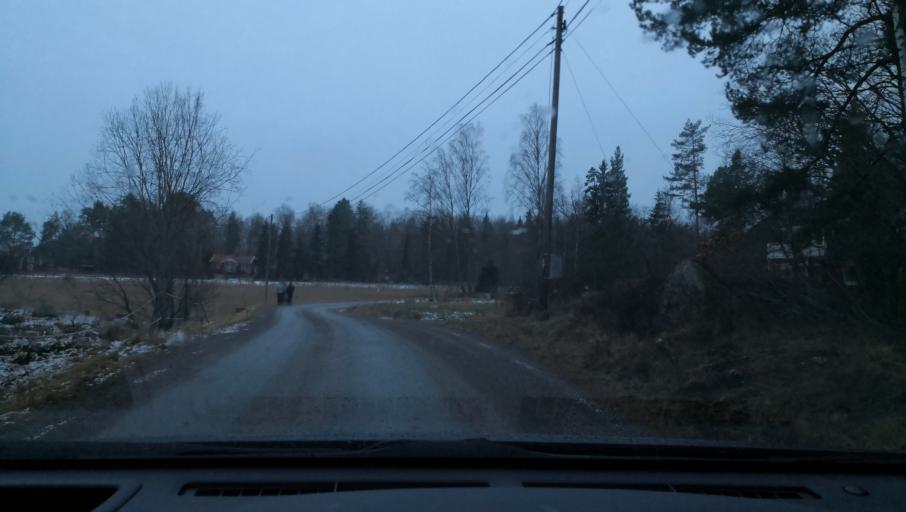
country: SE
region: Soedermanland
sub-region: Eskilstuna Kommun
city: Arla
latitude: 59.4478
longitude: 16.7820
